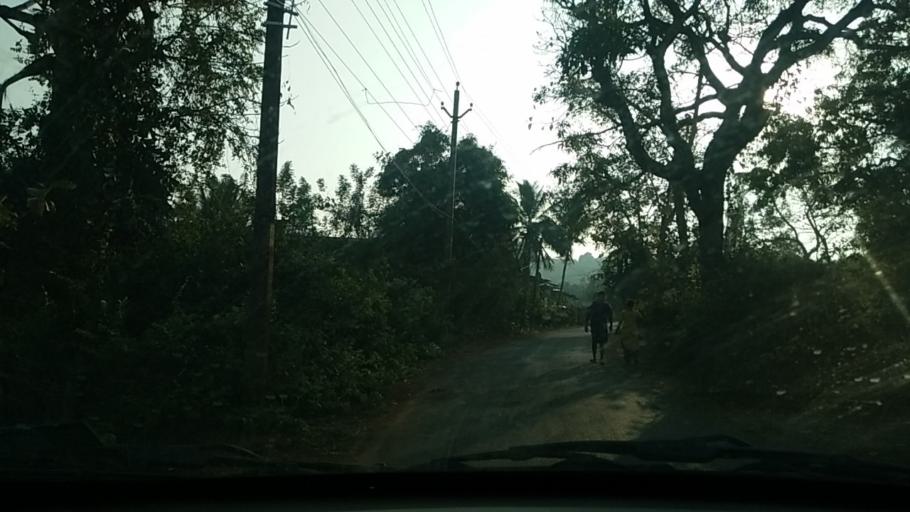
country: IN
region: Goa
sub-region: North Goa
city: Bambolim
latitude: 15.4596
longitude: 73.8728
